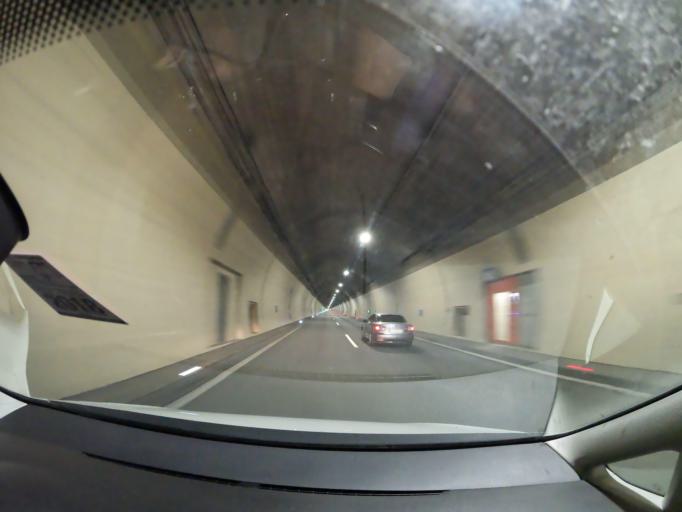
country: AT
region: Carinthia
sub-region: Politischer Bezirk Wolfsberg
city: Wolfsberg
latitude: 46.9023
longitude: 14.8207
